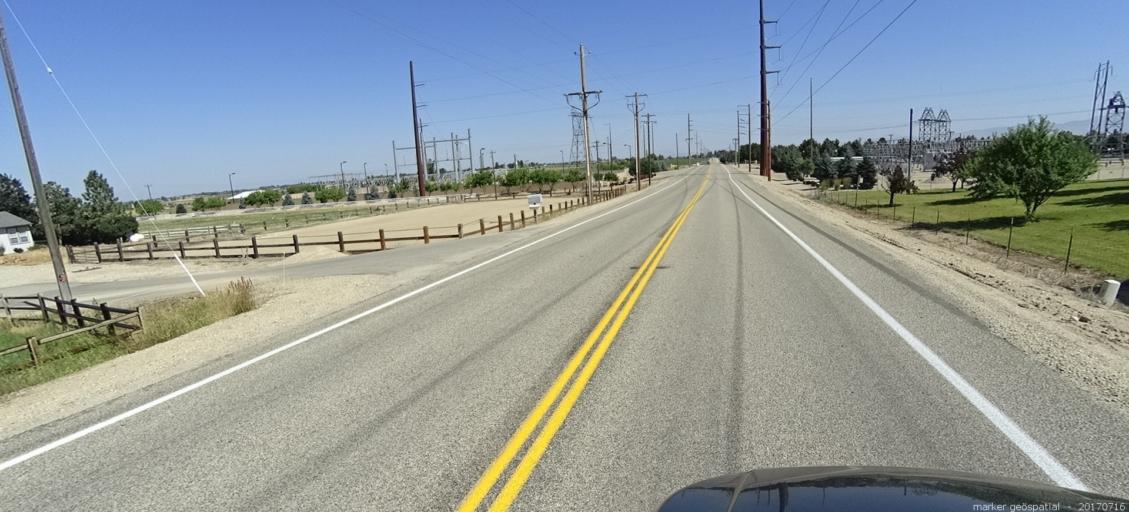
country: US
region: Idaho
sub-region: Ada County
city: Kuna
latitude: 43.5054
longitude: -116.3344
